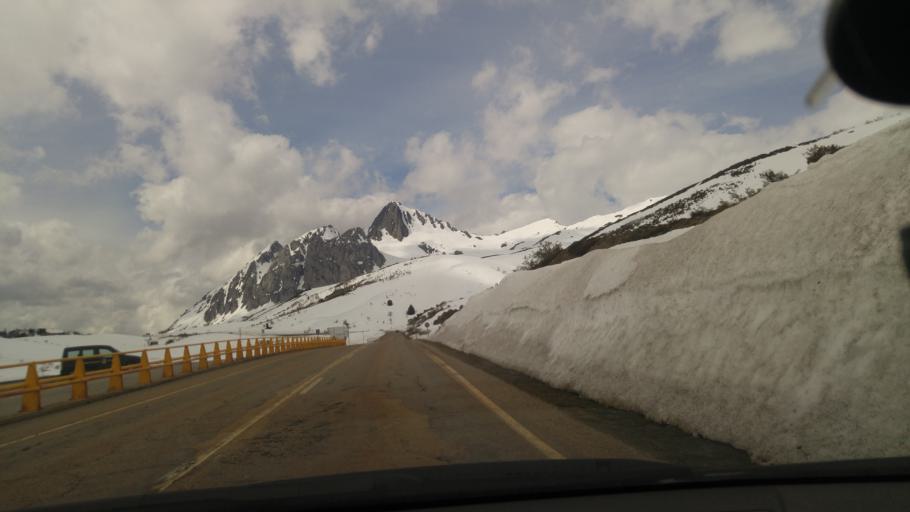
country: ES
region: Castille and Leon
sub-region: Provincia de Leon
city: Puebla de Lillo
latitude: 43.0641
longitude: -5.3778
